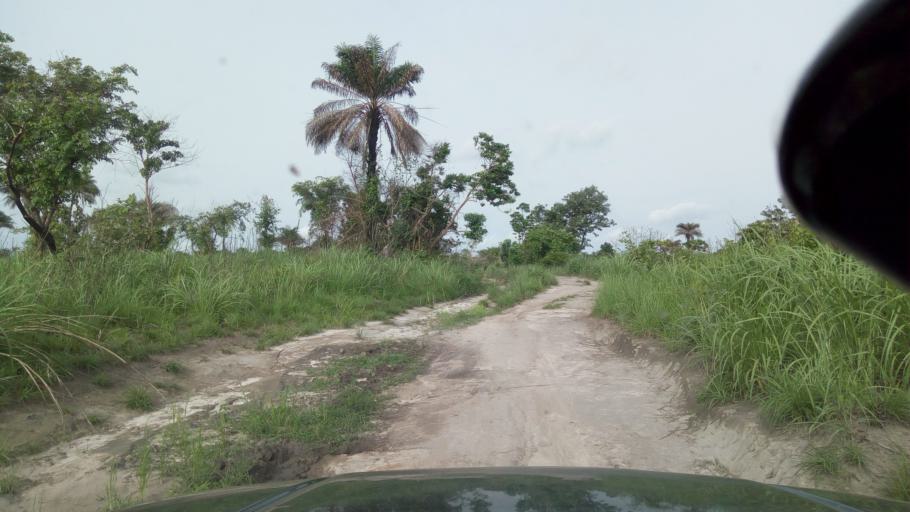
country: SL
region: Northern Province
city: Lunsar
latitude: 8.8490
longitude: -12.5354
